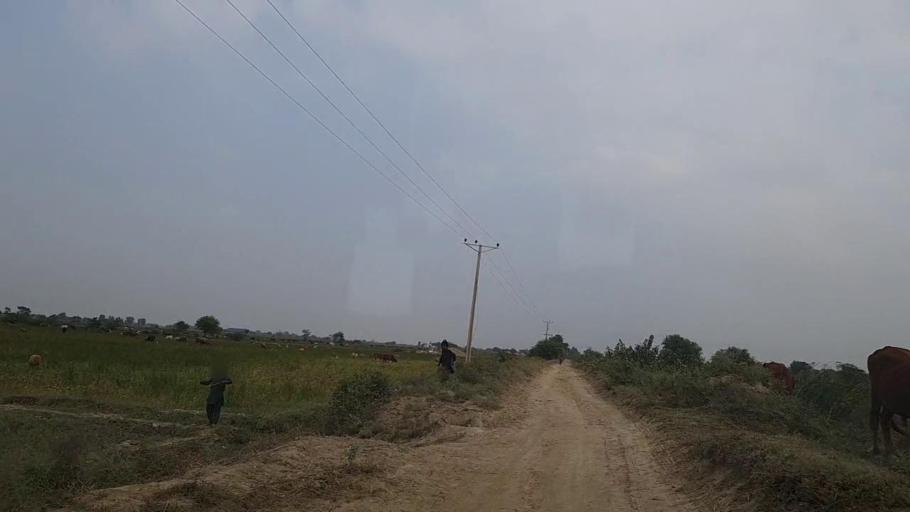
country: PK
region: Sindh
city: Mirpur Sakro
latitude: 24.6091
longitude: 67.7080
